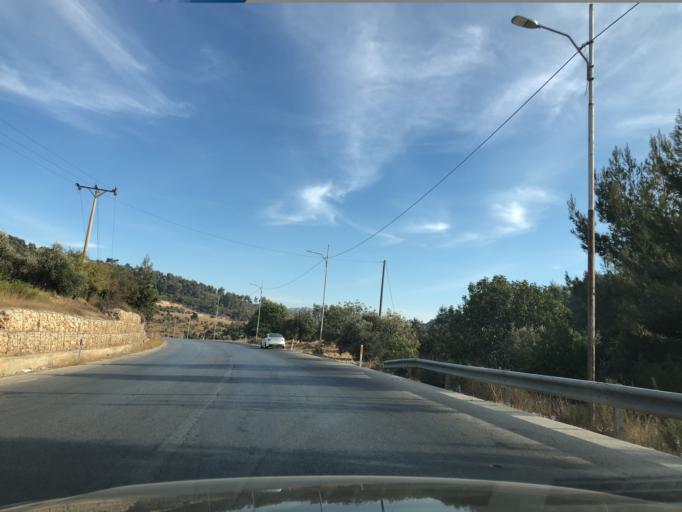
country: JO
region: Irbid
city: Sakib
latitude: 32.2877
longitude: 35.7922
